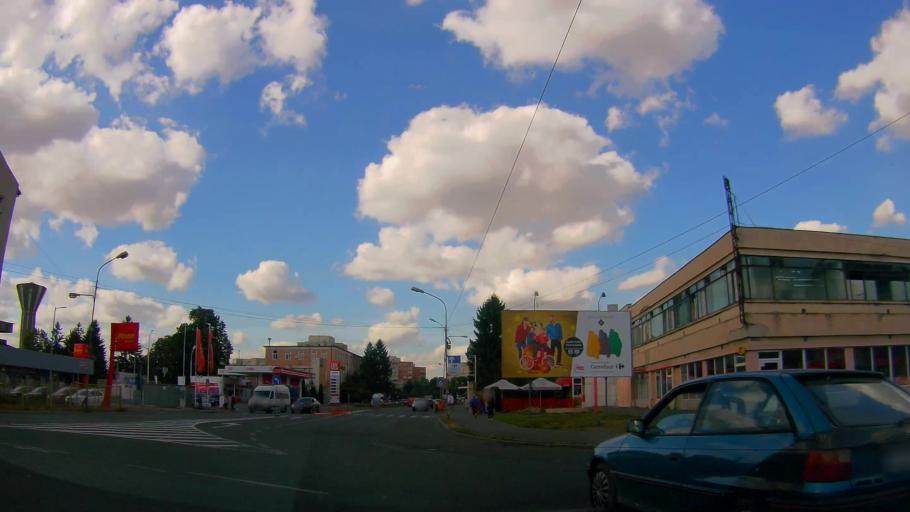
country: RO
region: Satu Mare
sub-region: Municipiul Satu Mare
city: Satu Mare
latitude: 47.7772
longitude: 22.8837
